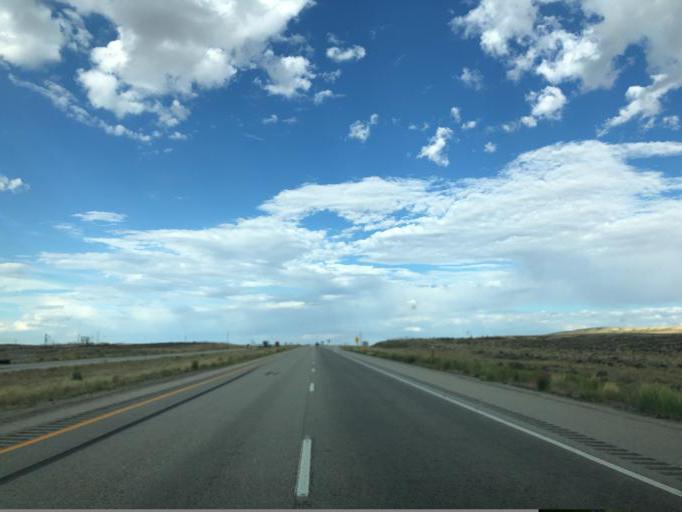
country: US
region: Wyoming
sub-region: Sweetwater County
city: Rock Springs
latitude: 41.6320
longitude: -108.2721
